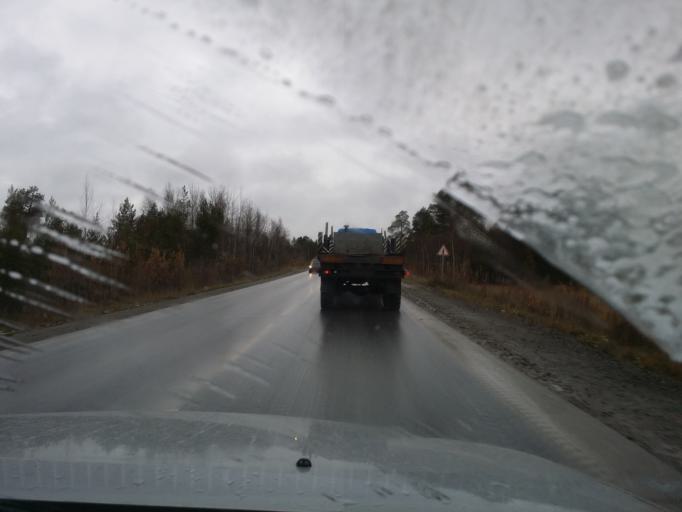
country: RU
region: Khanty-Mansiyskiy Avtonomnyy Okrug
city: Megion
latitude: 61.1366
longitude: 75.7648
